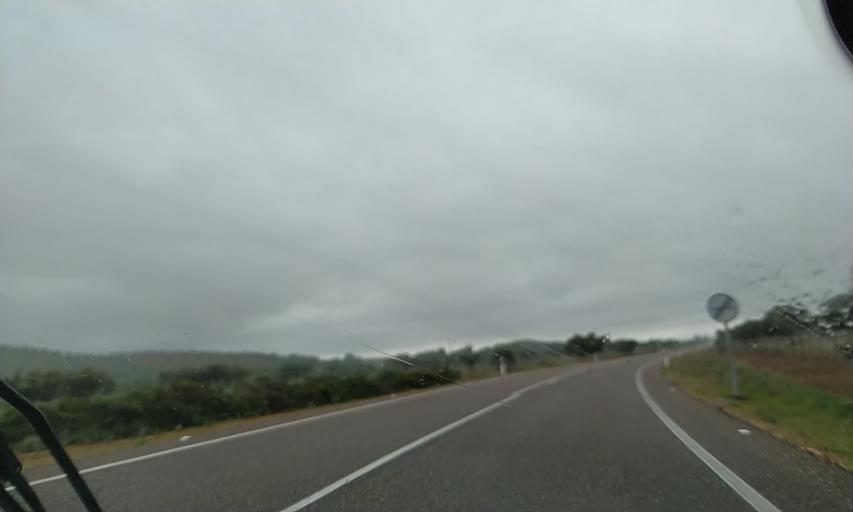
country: ES
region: Extremadura
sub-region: Provincia de Badajoz
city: La Roca de la Sierra
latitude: 39.0905
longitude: -6.7199
